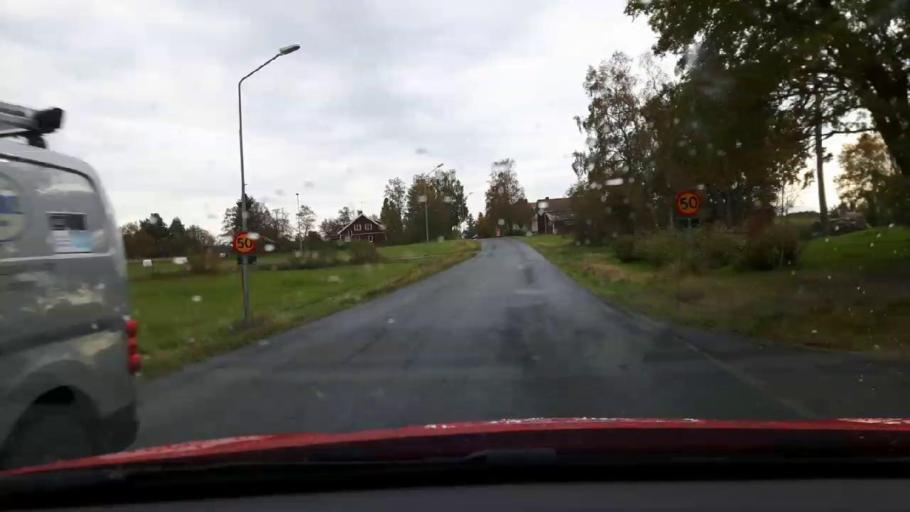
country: SE
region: Jaemtland
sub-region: Bergs Kommun
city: Hoverberg
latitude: 62.9219
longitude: 14.5167
